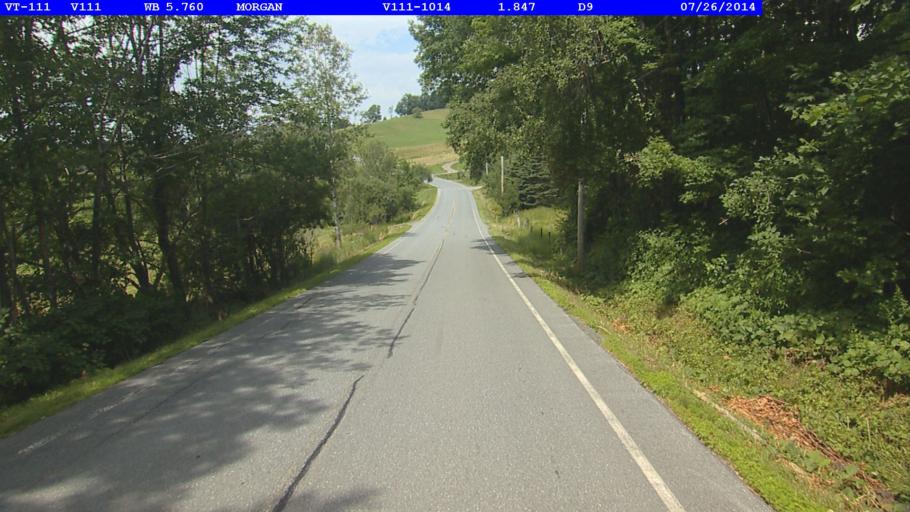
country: US
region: Vermont
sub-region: Orleans County
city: Newport
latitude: 44.9214
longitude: -72.0304
